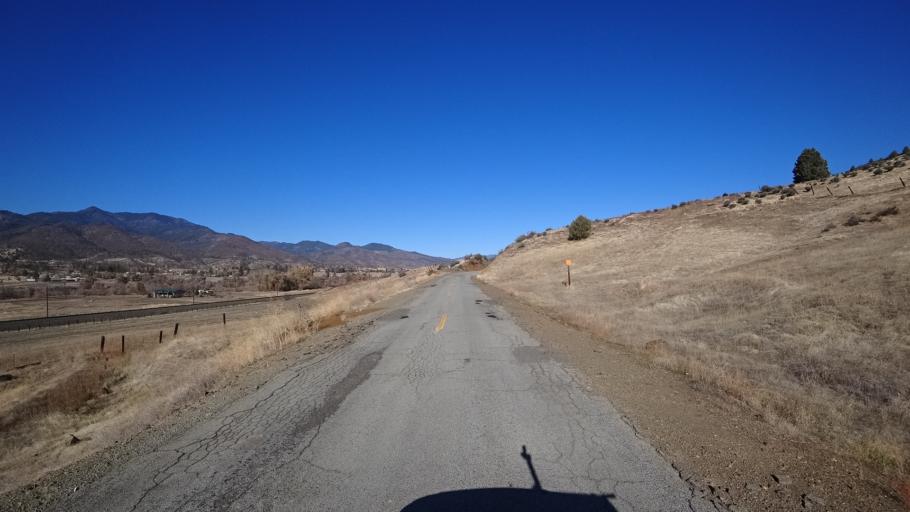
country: US
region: California
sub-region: Siskiyou County
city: Montague
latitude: 41.8993
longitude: -122.5435
